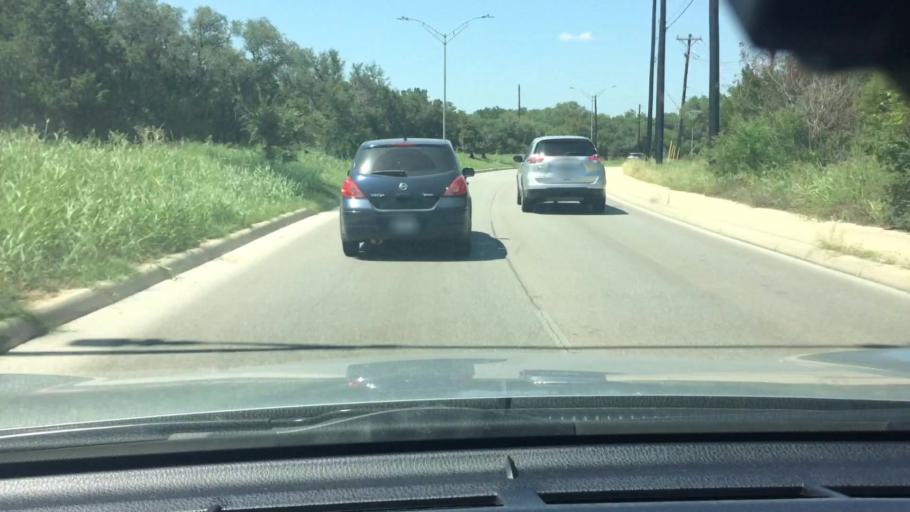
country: US
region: Texas
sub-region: Bexar County
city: Leon Valley
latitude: 29.4821
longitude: -98.7001
